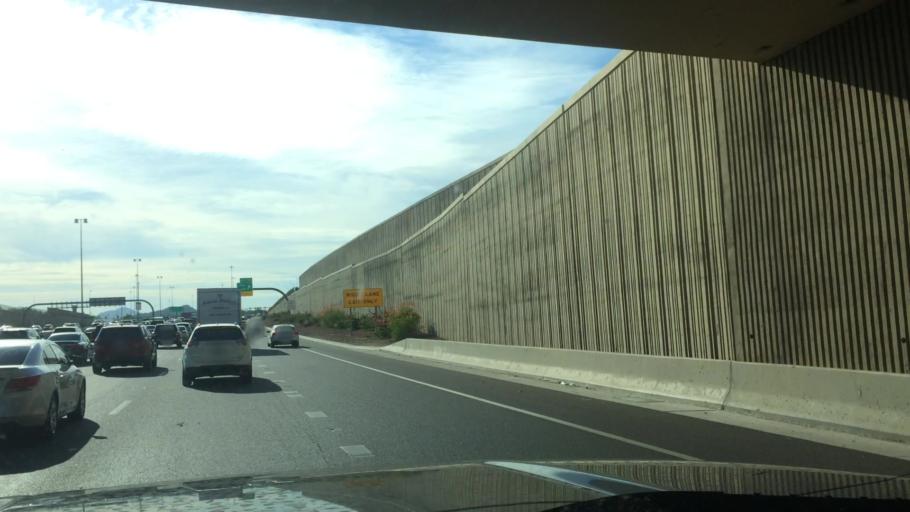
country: US
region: Arizona
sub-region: Maricopa County
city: Glendale
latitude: 33.6690
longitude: -112.0913
